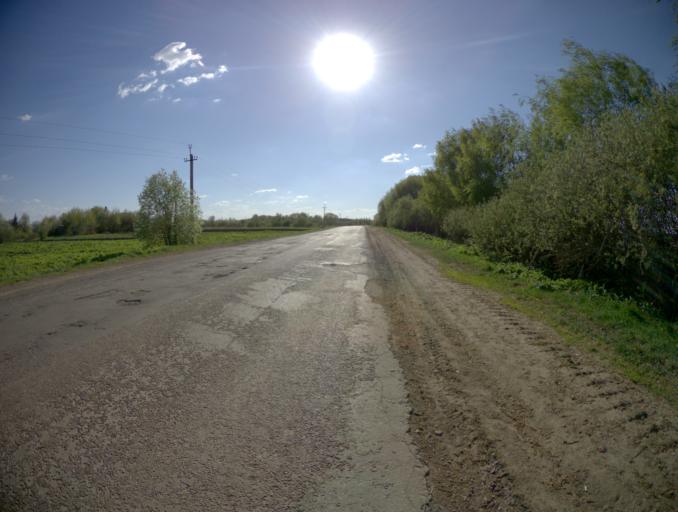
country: RU
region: Ivanovo
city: Gavrilov Posad
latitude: 56.3447
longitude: 40.1944
